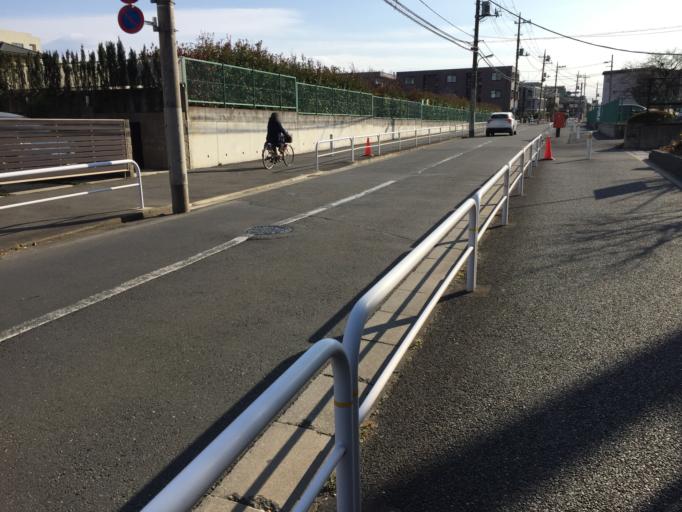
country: JP
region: Tokyo
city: Mitaka-shi
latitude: 35.6655
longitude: 139.6079
